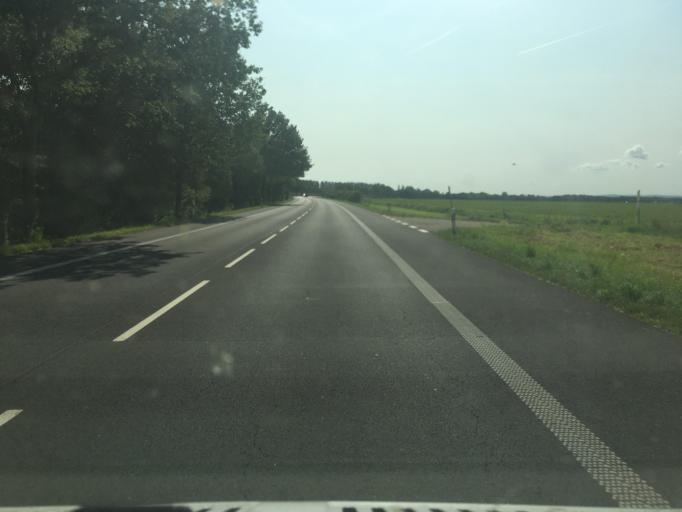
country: DE
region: North Rhine-Westphalia
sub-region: Regierungsbezirk Koln
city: Norvenich
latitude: 50.7489
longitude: 6.6519
